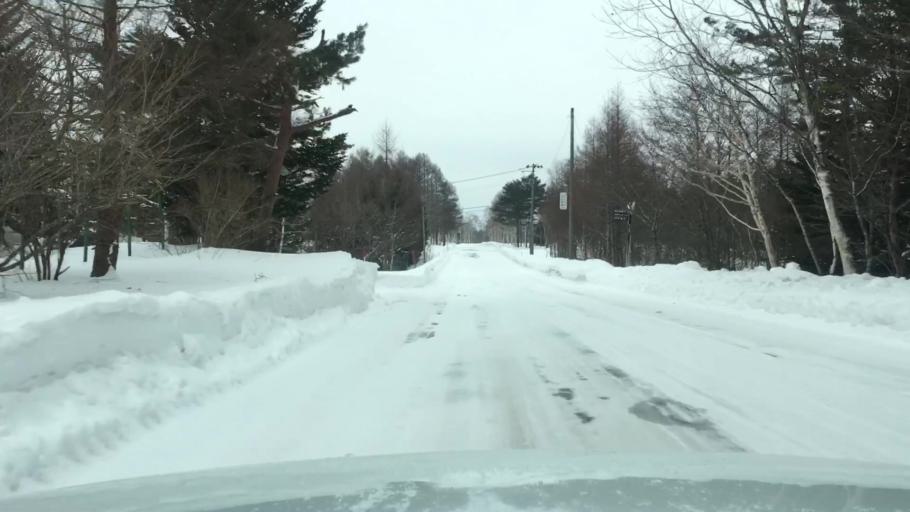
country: JP
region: Akita
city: Hanawa
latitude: 40.0044
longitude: 140.9810
